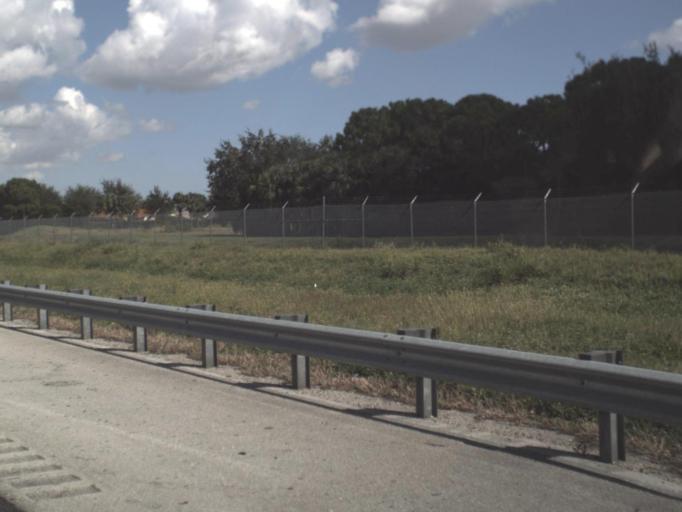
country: US
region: Florida
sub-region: Palm Beach County
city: Villages of Oriole
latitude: 26.4891
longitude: -80.1724
